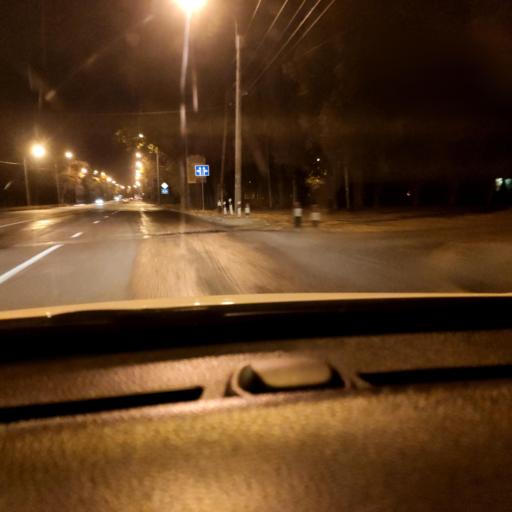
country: RU
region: Voronezj
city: Maslovka
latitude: 51.6097
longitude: 39.2452
